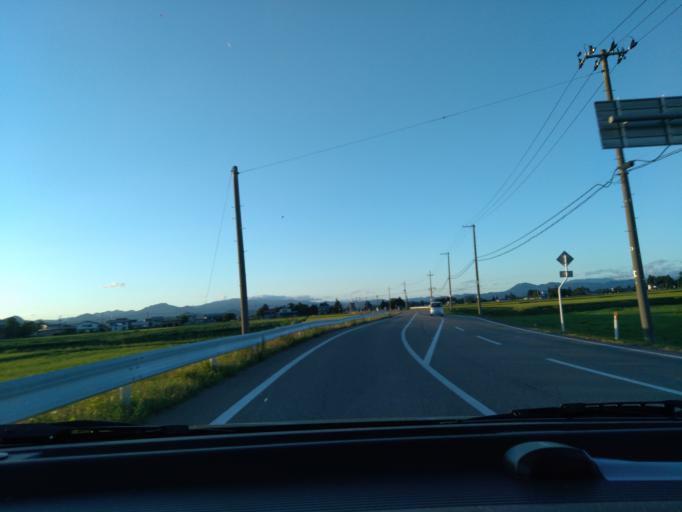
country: JP
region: Akita
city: Kakunodatemachi
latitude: 39.5163
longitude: 140.5585
